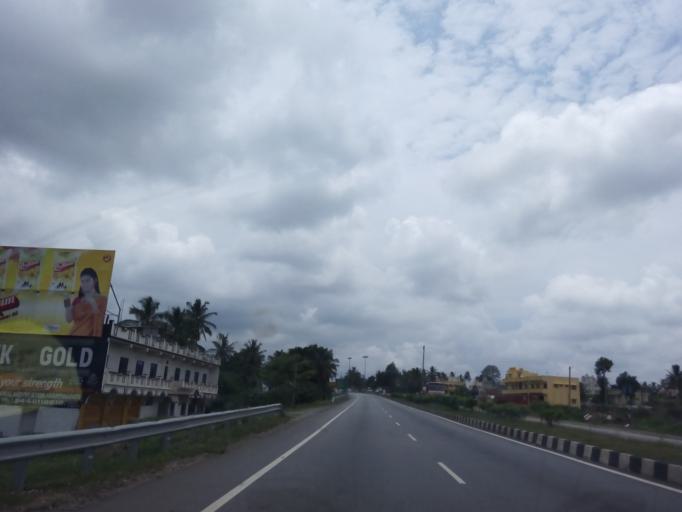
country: IN
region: Karnataka
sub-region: Hassan
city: Hassan
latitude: 13.0012
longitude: 76.1418
